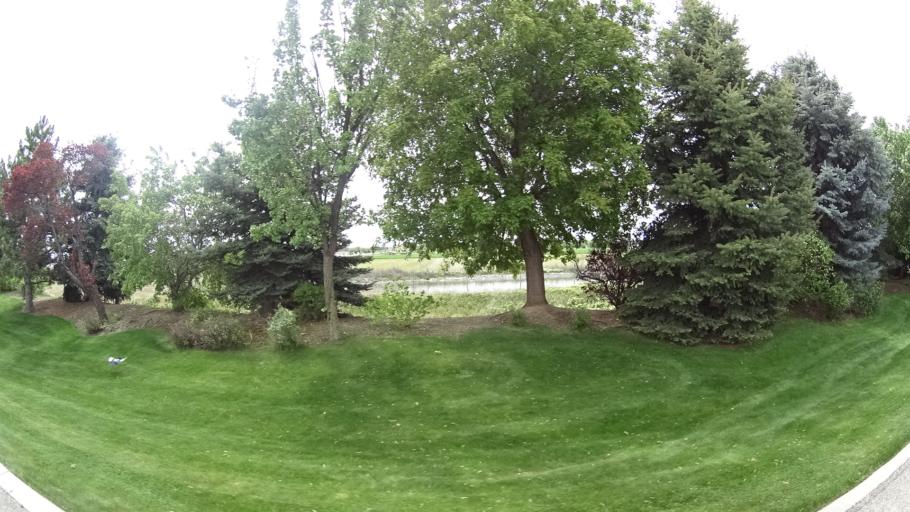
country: US
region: Idaho
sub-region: Ada County
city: Kuna
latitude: 43.5391
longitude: -116.3955
